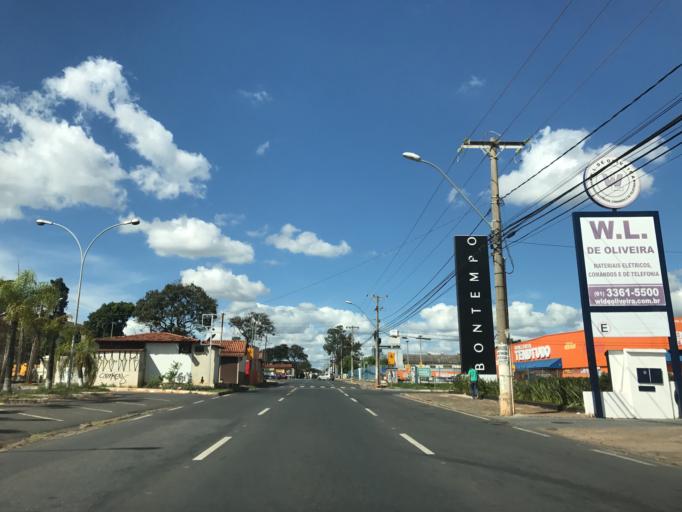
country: BR
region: Federal District
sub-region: Brasilia
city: Brasilia
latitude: -15.8041
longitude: -47.9589
